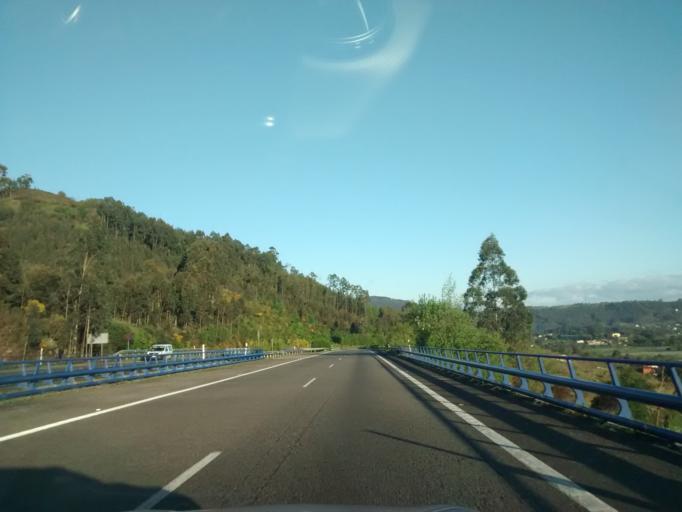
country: ES
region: Asturias
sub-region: Province of Asturias
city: Villaviciosa
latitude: 43.4969
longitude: -5.3764
